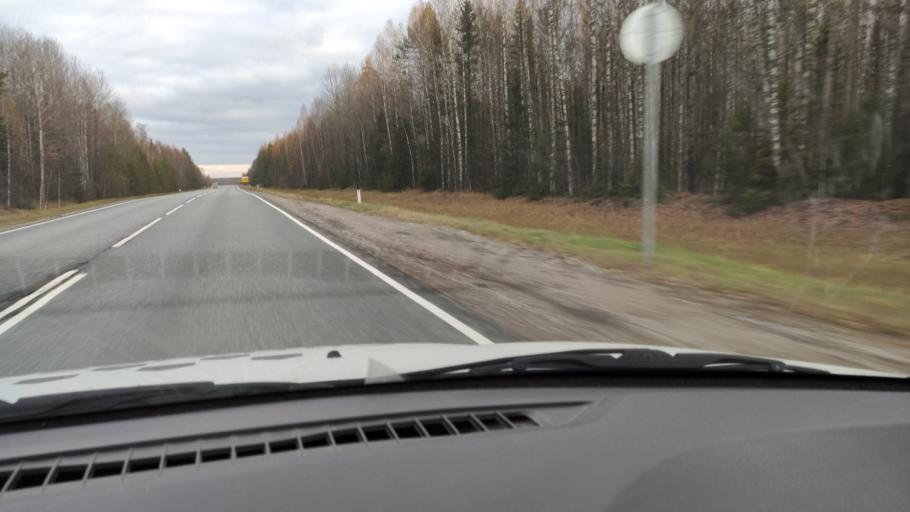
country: RU
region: Kirov
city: Dubrovka
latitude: 58.8970
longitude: 51.3206
